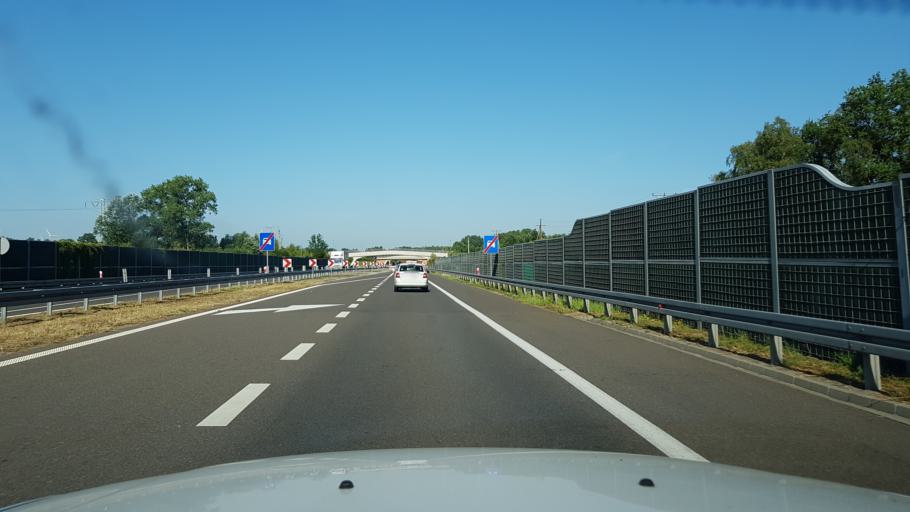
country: PL
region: West Pomeranian Voivodeship
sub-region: Powiat goleniowski
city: Przybiernow
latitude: 53.8425
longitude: 14.7225
